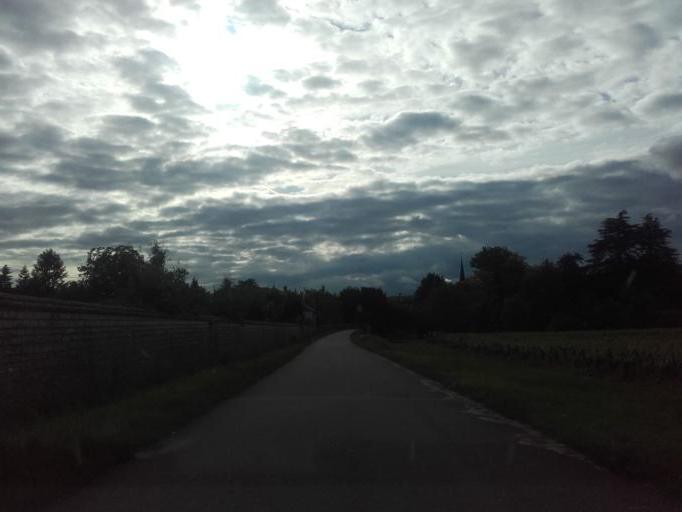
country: FR
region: Bourgogne
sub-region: Departement de Saone-et-Loire
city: Mellecey
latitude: 46.8313
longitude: 4.7407
